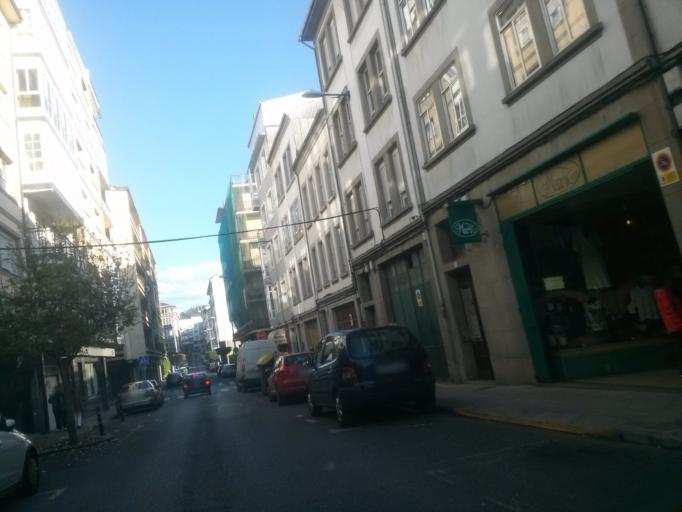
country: ES
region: Galicia
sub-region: Provincia de Lugo
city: Lugo
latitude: 43.0147
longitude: -7.5657
